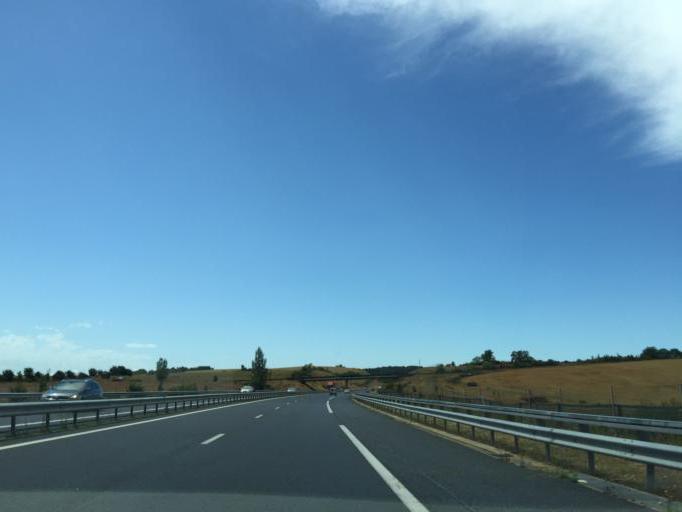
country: FR
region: Midi-Pyrenees
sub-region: Departement de l'Aveyron
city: Severac-le-Chateau
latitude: 44.2648
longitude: 3.0776
